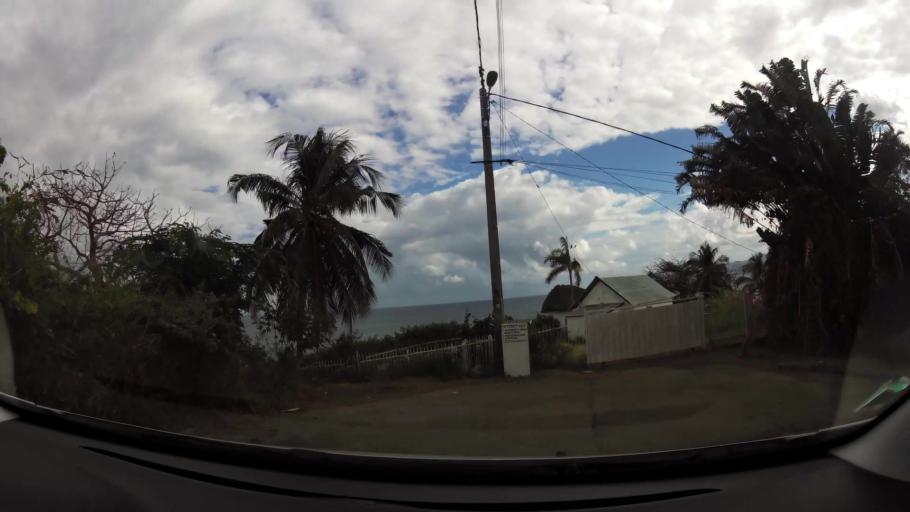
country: YT
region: Sada
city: Sada
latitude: -12.8524
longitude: 45.0930
